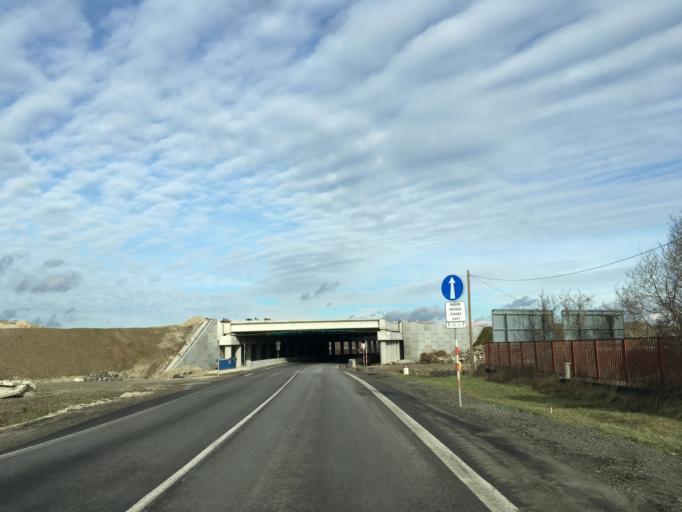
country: AT
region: Burgenland
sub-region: Politischer Bezirk Neusiedl am See
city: Kittsee
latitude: 48.0734
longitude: 17.1195
